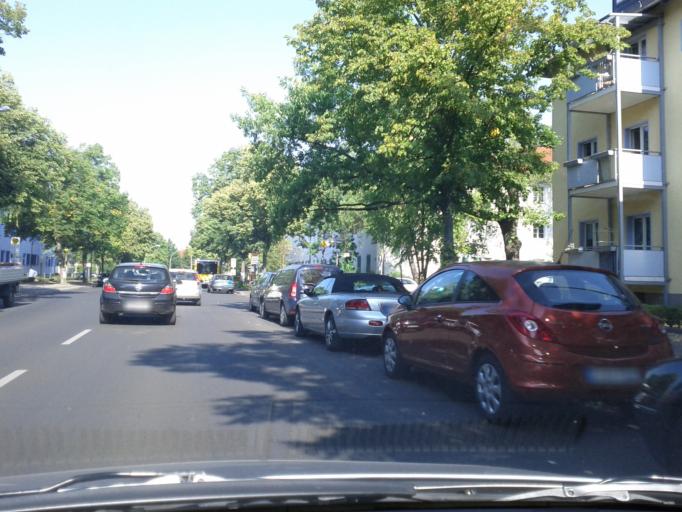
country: DE
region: Berlin
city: Kopenick Bezirk
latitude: 52.4664
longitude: 13.5762
